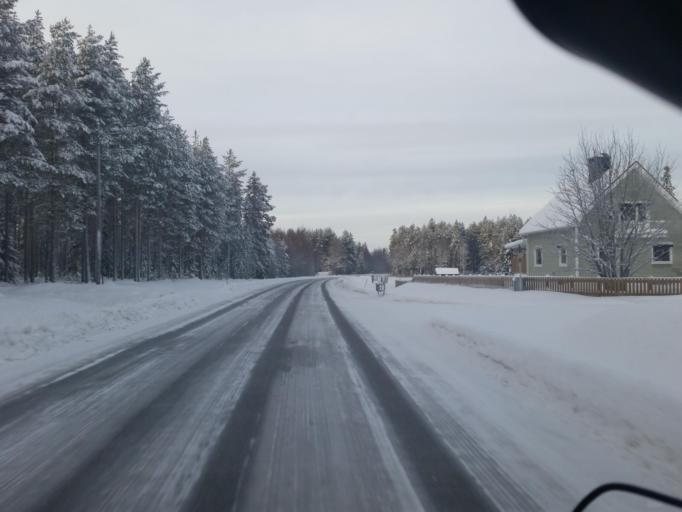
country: SE
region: Norrbotten
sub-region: Pitea Kommun
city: Norrfjarden
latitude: 65.4380
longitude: 21.4718
